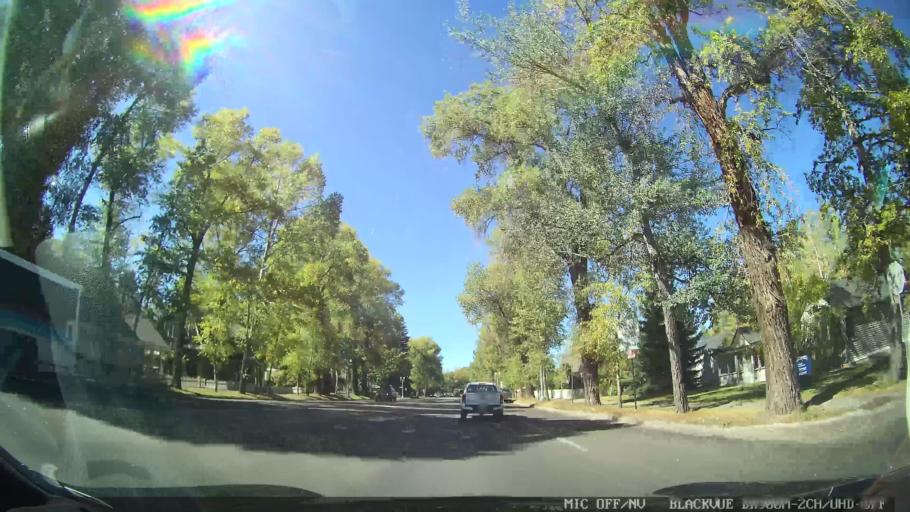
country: US
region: Colorado
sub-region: Pitkin County
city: Aspen
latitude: 39.1926
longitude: -106.8284
